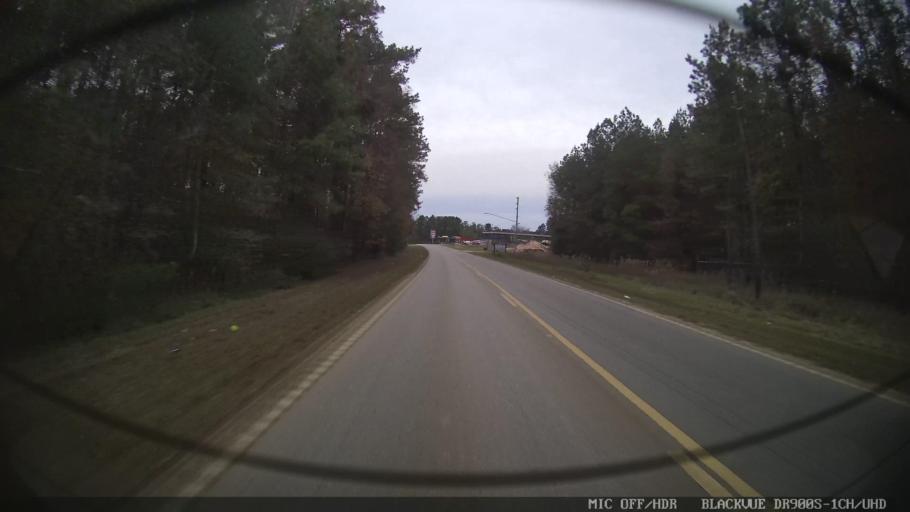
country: US
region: Mississippi
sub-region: Clarke County
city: Stonewall
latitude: 32.0561
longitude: -88.8999
